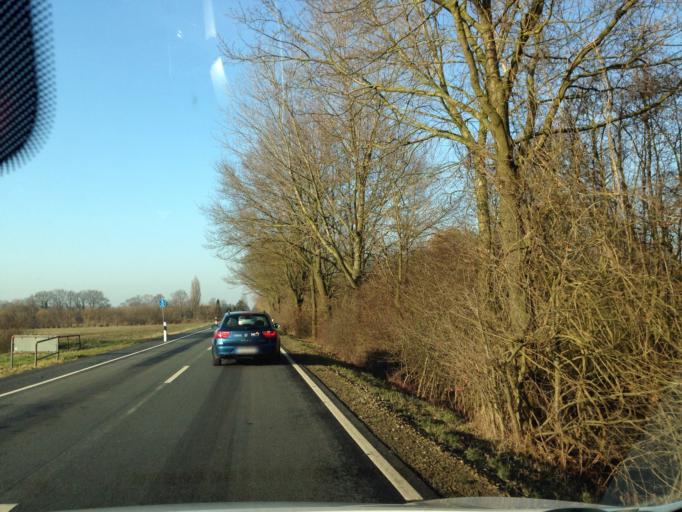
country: DE
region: North Rhine-Westphalia
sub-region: Regierungsbezirk Munster
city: Muenster
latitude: 52.0199
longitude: 7.6023
